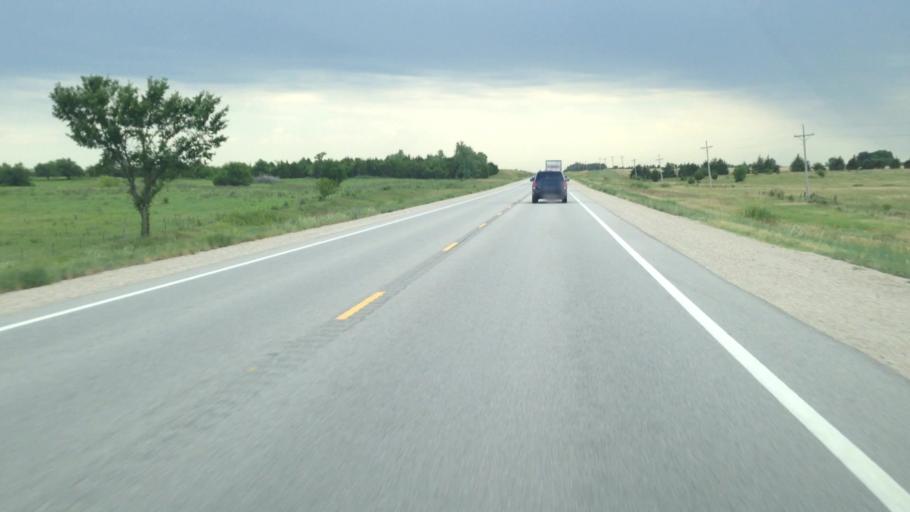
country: US
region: Kansas
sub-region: Coffey County
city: Burlington
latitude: 38.3287
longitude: -95.7290
